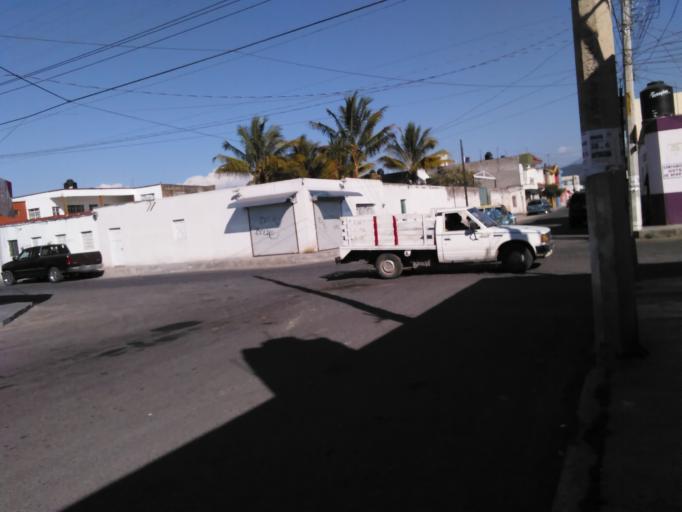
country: MX
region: Nayarit
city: Tepic
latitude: 21.5249
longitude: -104.8897
